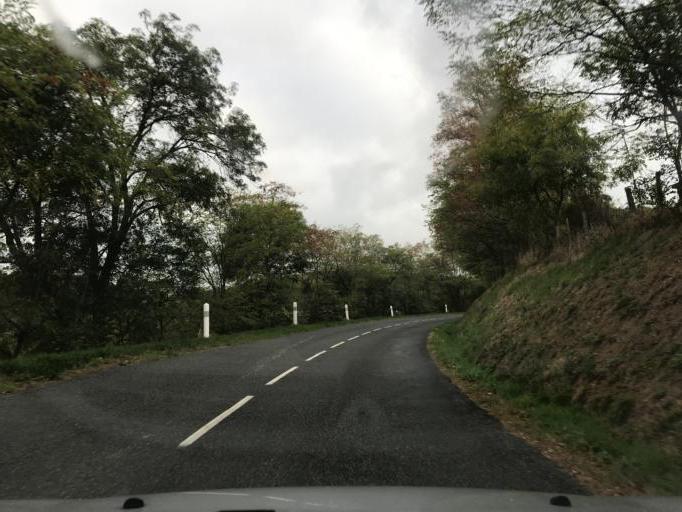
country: FR
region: Rhone-Alpes
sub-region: Departement du Rhone
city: Le Perreon
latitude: 46.0192
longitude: 4.5726
